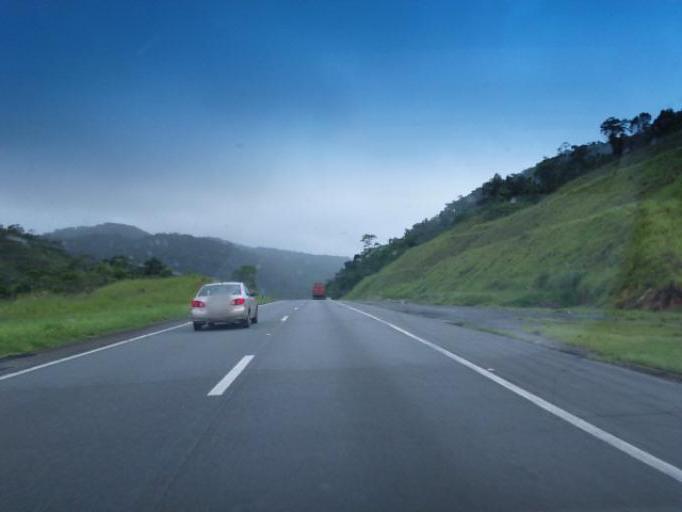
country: BR
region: Sao Paulo
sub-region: Cajati
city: Cajati
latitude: -24.9050
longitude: -48.2487
